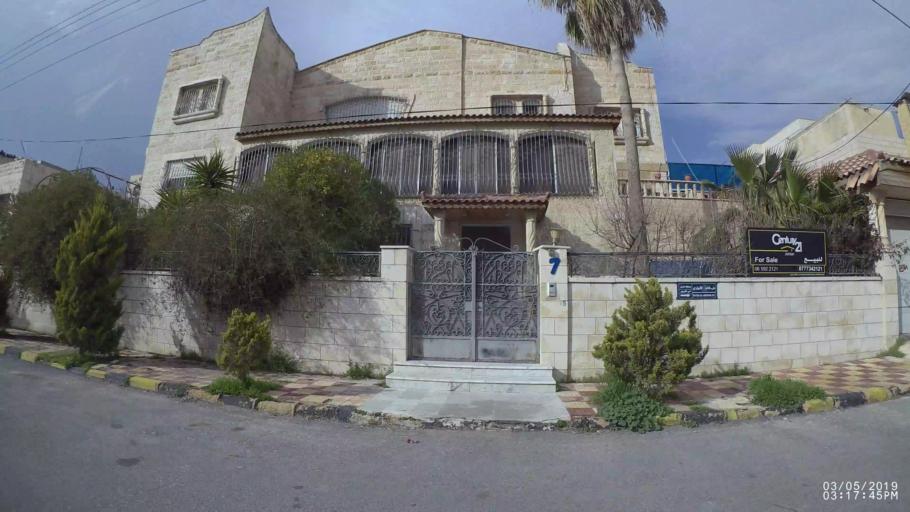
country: JO
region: Amman
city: Amman
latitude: 32.0036
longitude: 35.9454
